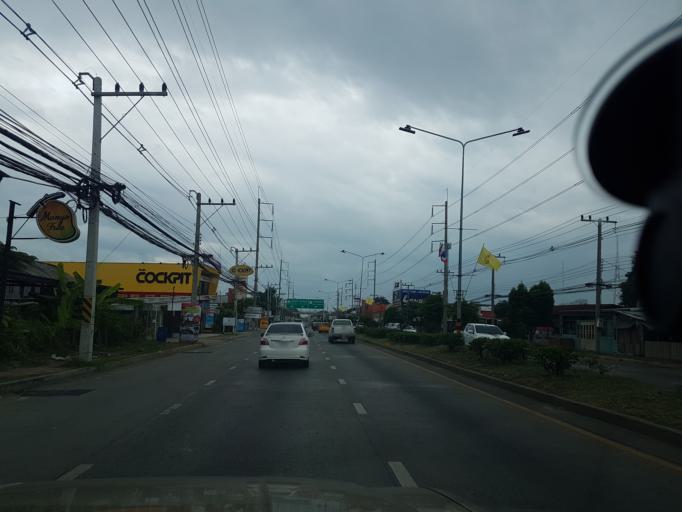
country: TH
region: Lop Buri
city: Lop Buri
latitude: 14.7995
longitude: 100.6584
